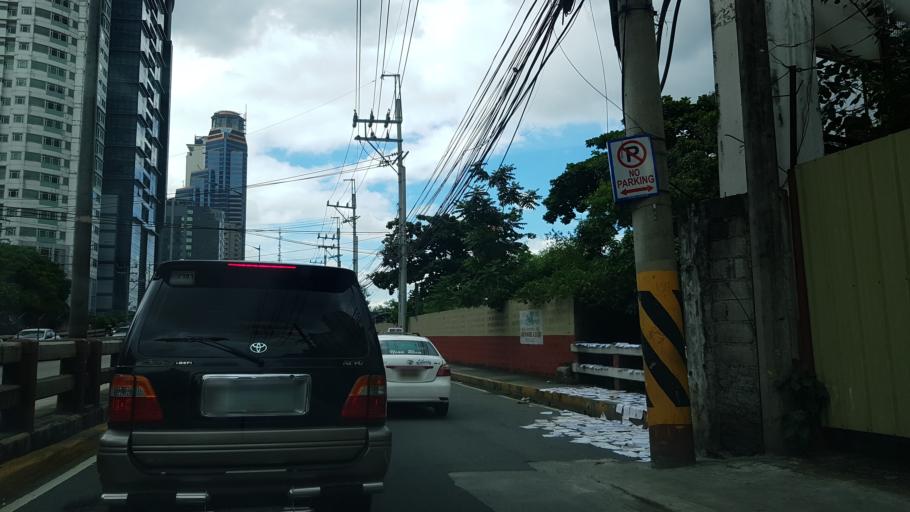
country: PH
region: Metro Manila
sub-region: Pasig
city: Pasig City
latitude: 14.5819
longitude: 121.0639
